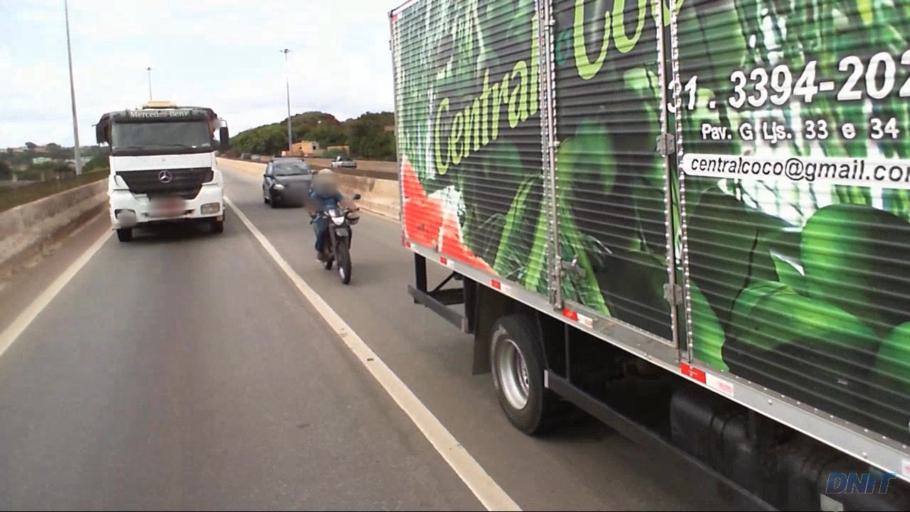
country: BR
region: Minas Gerais
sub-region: Belo Horizonte
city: Belo Horizonte
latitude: -19.8648
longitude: -43.9279
